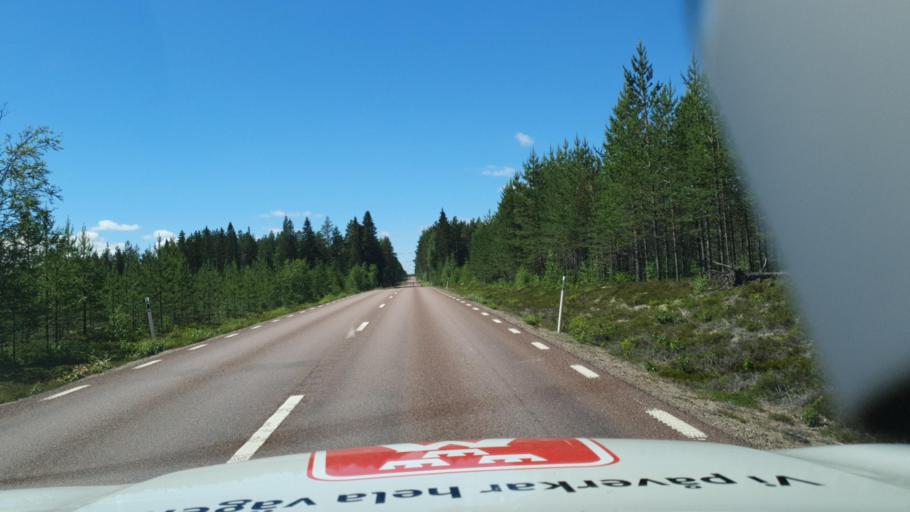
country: SE
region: Jaemtland
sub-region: Harjedalens Kommun
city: Sveg
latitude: 62.0519
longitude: 14.5158
